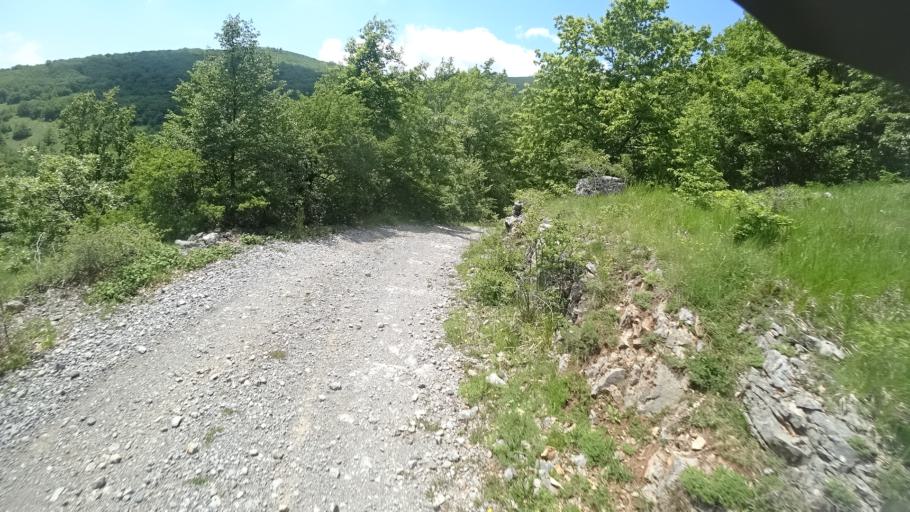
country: HR
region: Zadarska
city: Gracac
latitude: 44.4473
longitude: 15.9140
